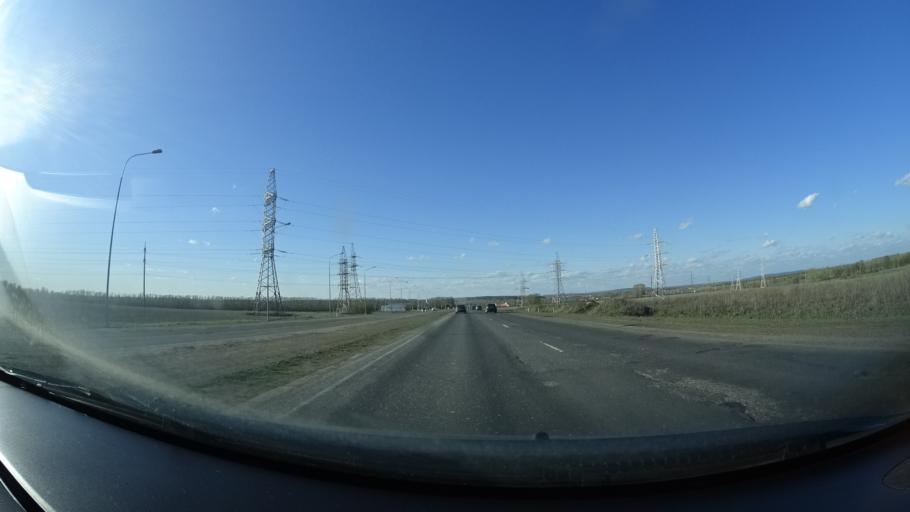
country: RU
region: Bashkortostan
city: Kabakovo
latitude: 54.4793
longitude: 55.9101
